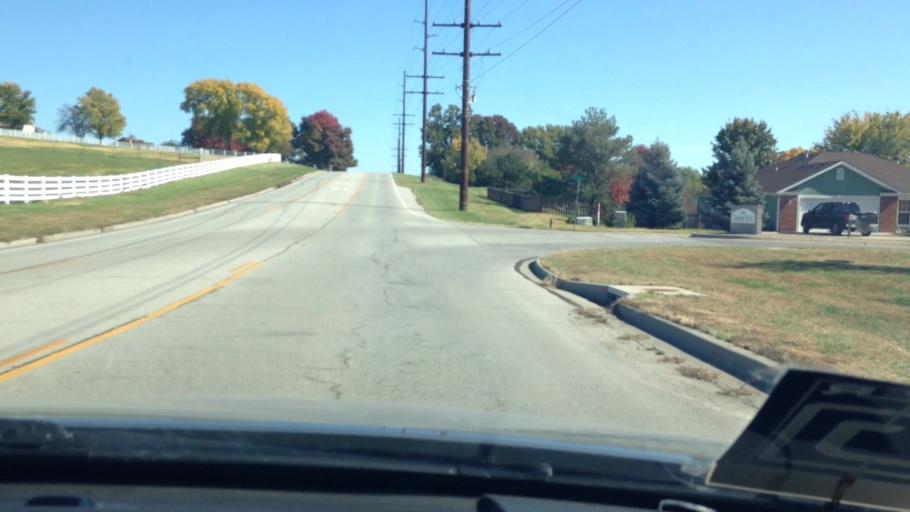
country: US
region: Missouri
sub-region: Platte County
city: Platte City
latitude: 39.3394
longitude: -94.7679
